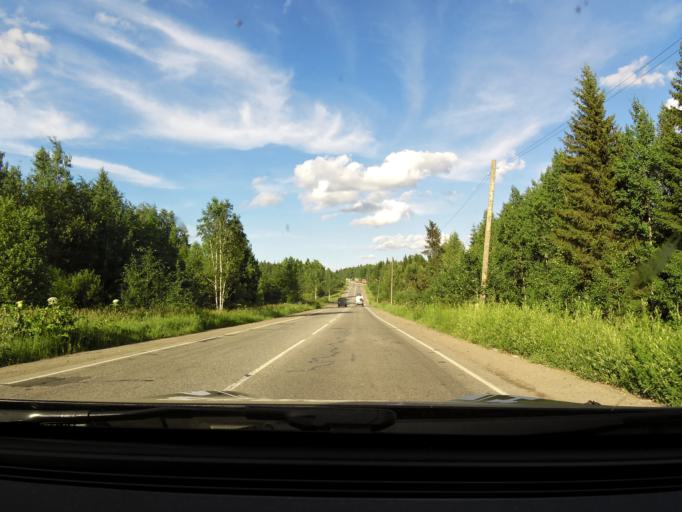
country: RU
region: Kirov
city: Omutninsk
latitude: 58.6977
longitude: 52.2259
